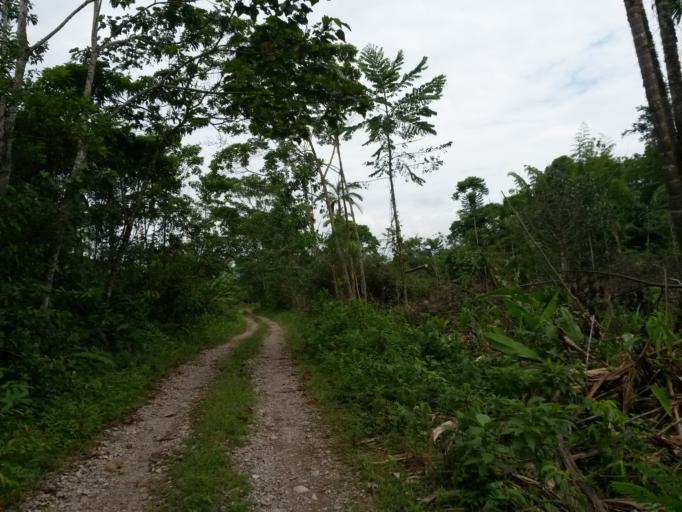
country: CO
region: Putumayo
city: Puerto Guzman
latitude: 1.0197
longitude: -76.3732
